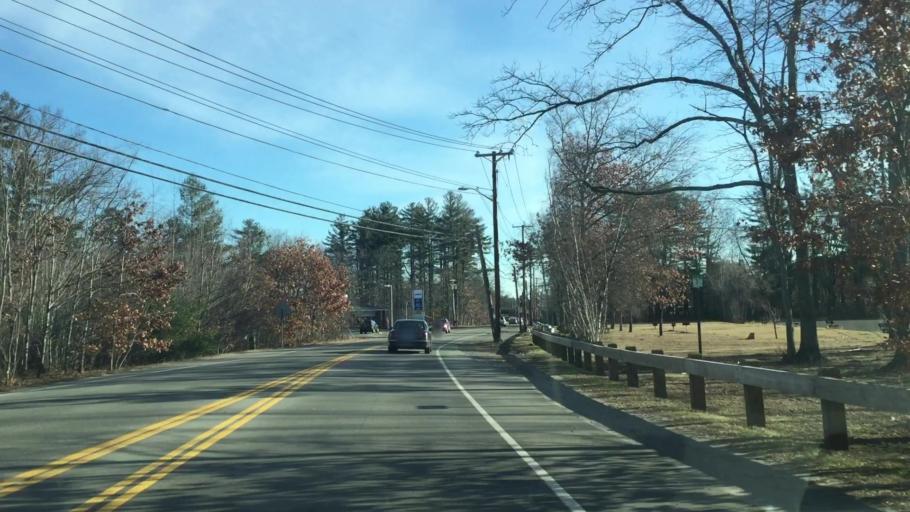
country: US
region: New Hampshire
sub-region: Rockingham County
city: Salem
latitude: 42.7651
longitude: -71.2454
